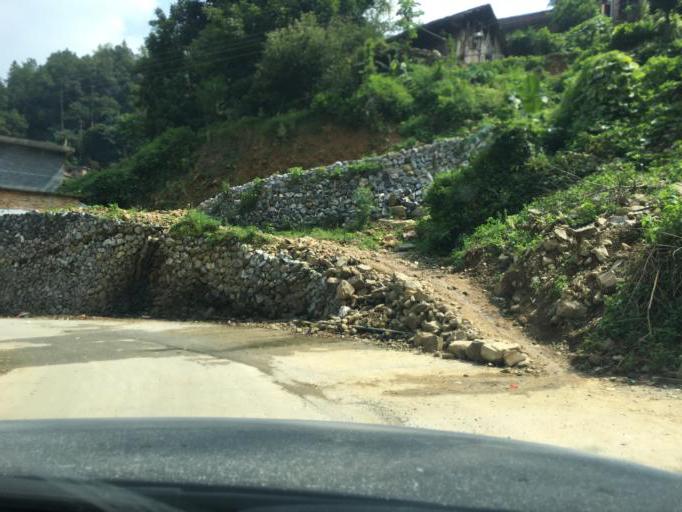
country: CN
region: Guangxi Zhuangzu Zizhiqu
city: Tongle
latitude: 25.2942
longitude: 106.2669
